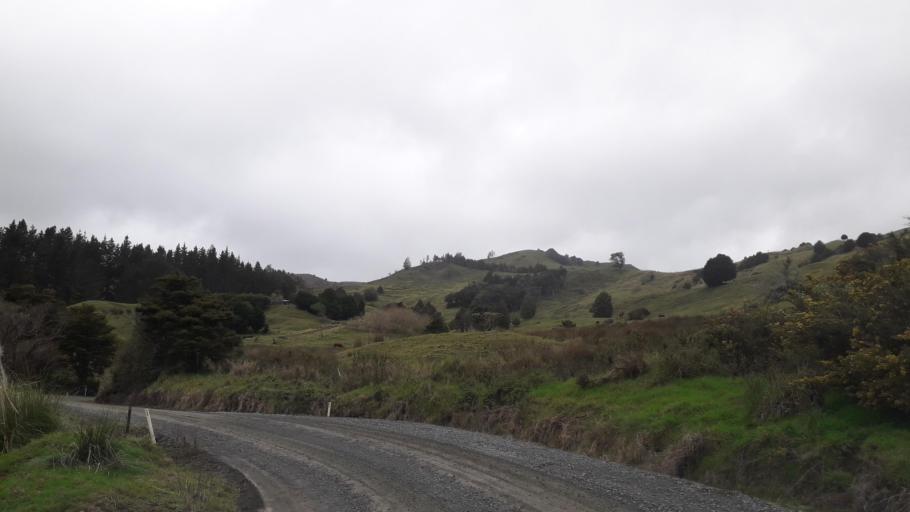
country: NZ
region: Northland
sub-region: Far North District
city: Kerikeri
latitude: -35.1324
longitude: 173.7377
